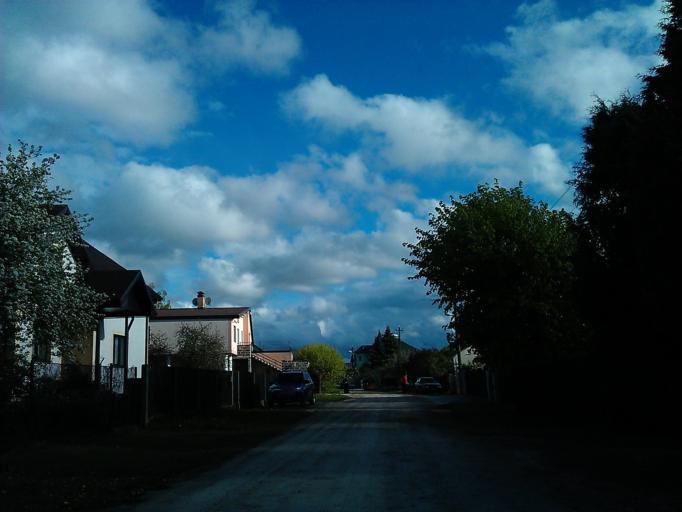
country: LV
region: Adazi
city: Adazi
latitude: 57.0726
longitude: 24.3258
